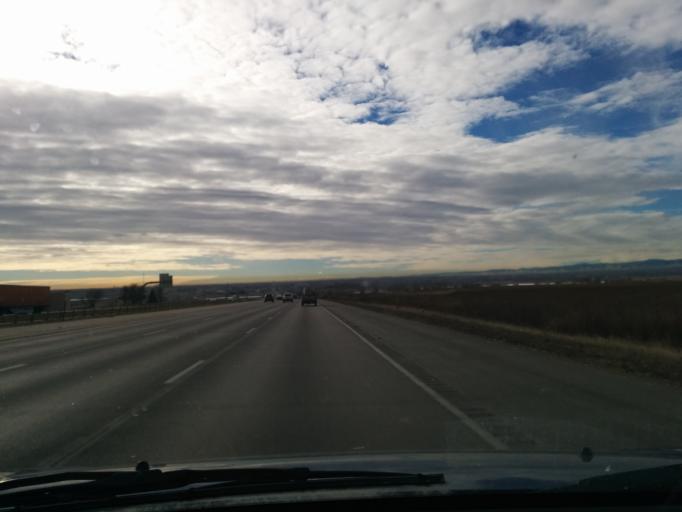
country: US
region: Colorado
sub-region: Weld County
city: Mead
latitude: 40.1876
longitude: -104.9805
